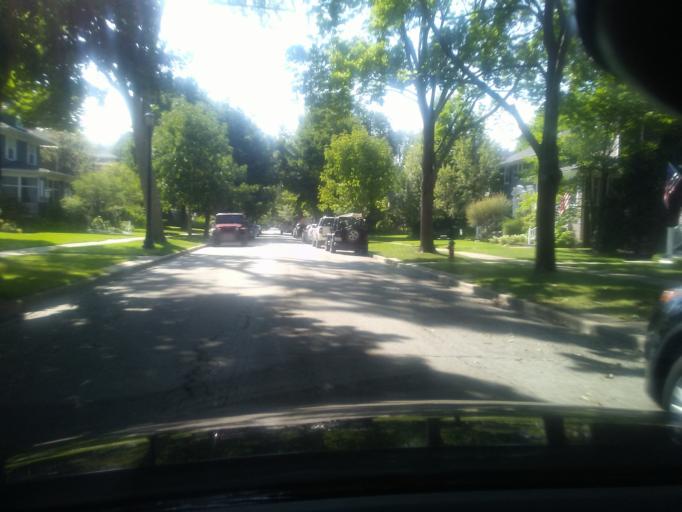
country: US
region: Illinois
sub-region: Cook County
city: Wilmette
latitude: 42.0633
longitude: -87.7092
